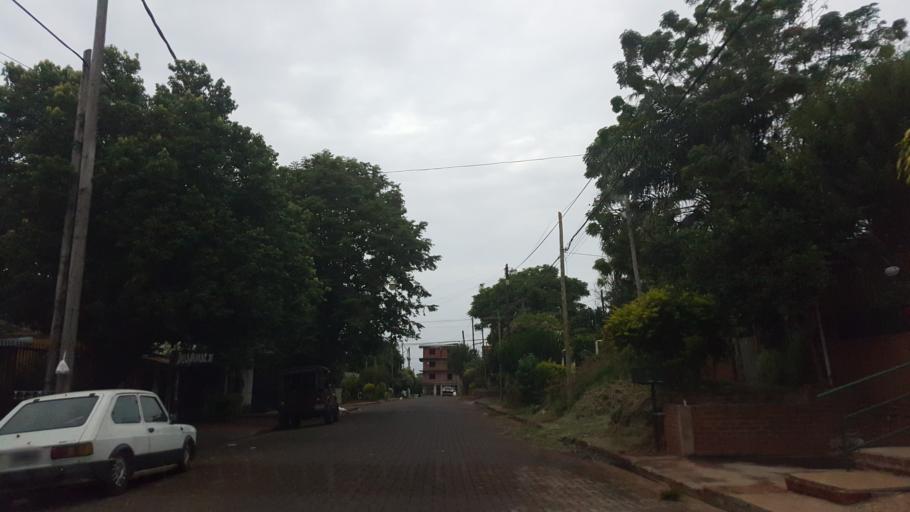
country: AR
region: Misiones
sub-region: Departamento de Capital
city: Posadas
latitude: -27.4021
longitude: -55.9079
